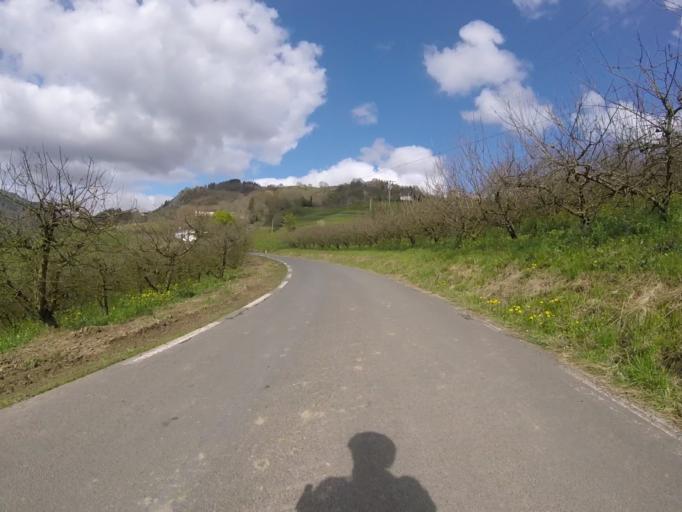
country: ES
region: Basque Country
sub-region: Provincia de Guipuzcoa
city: Tolosa
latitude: 43.1272
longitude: -2.0974
